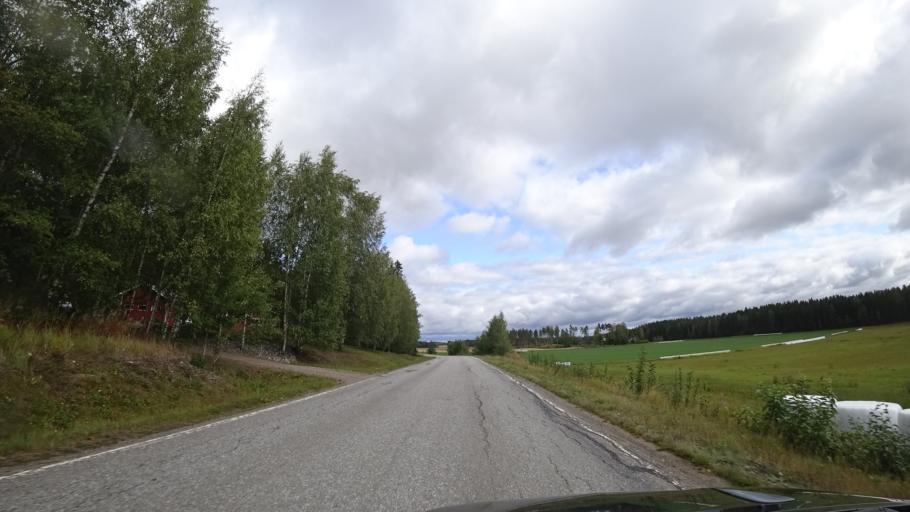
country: FI
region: Haeme
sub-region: Riihimaeki
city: Oitti
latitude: 60.9063
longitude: 25.0417
